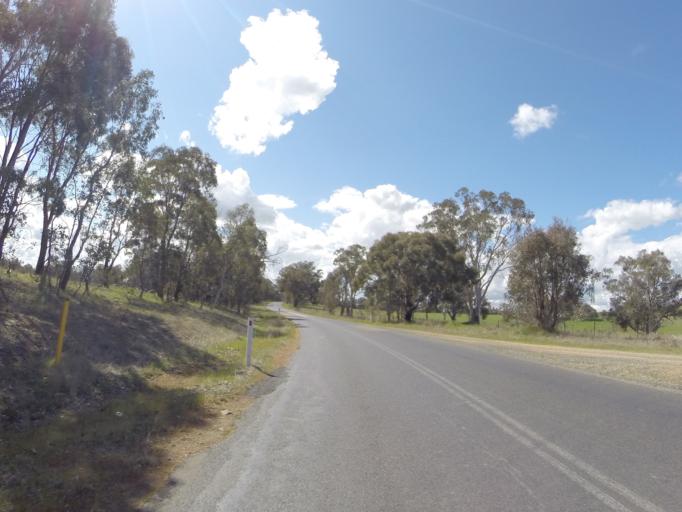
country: AU
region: New South Wales
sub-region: Yass Valley
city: Yass
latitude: -34.9804
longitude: 148.8553
